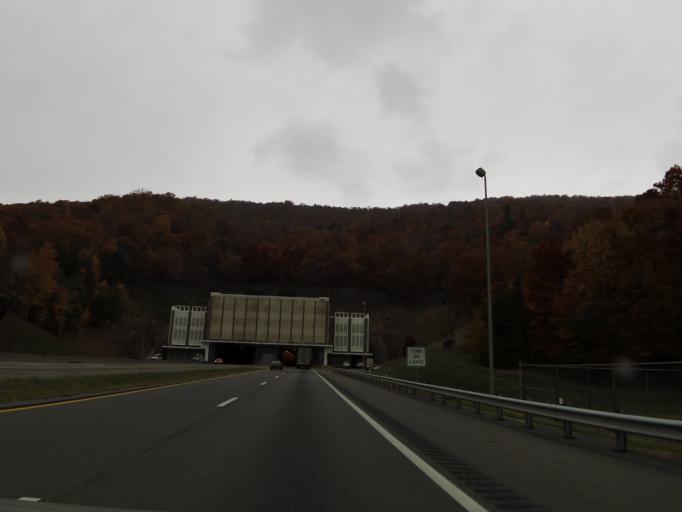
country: US
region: Virginia
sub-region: Bland County
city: Bland
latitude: 37.0345
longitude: -81.1247
